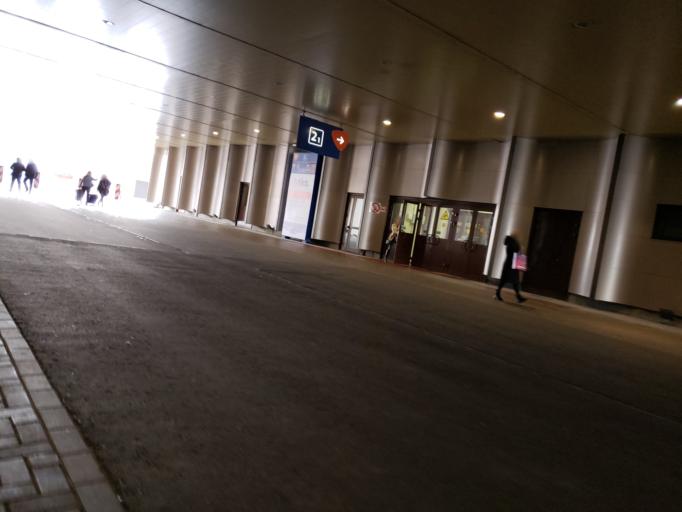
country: RU
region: Moskovskaya
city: Presnenskiy
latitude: 55.7515
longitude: 37.5438
